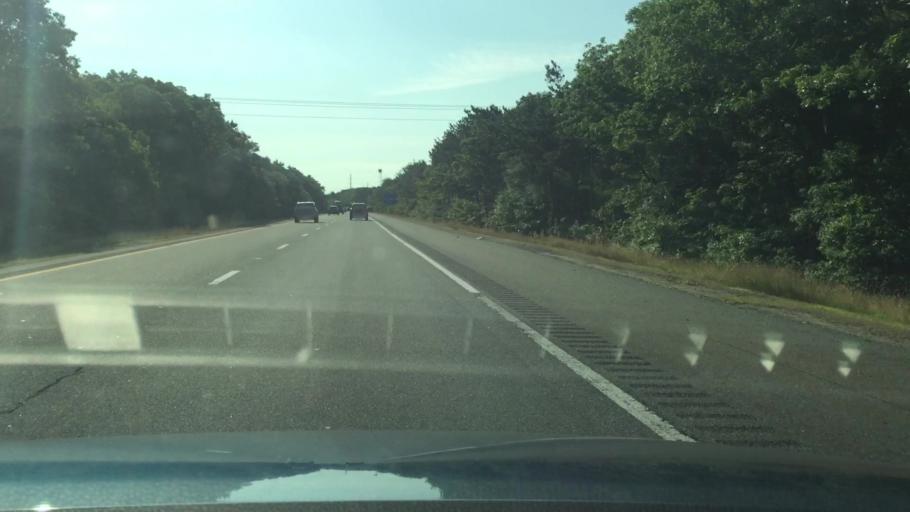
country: US
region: Massachusetts
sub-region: Barnstable County
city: Barnstable
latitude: 41.6878
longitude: -70.3046
